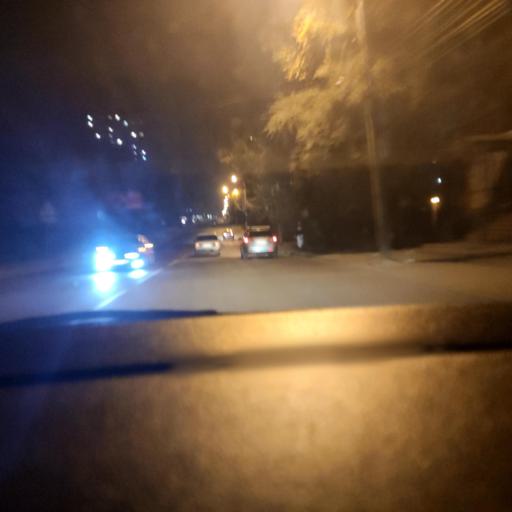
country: RU
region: Voronezj
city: Voronezh
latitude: 51.6690
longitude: 39.1521
